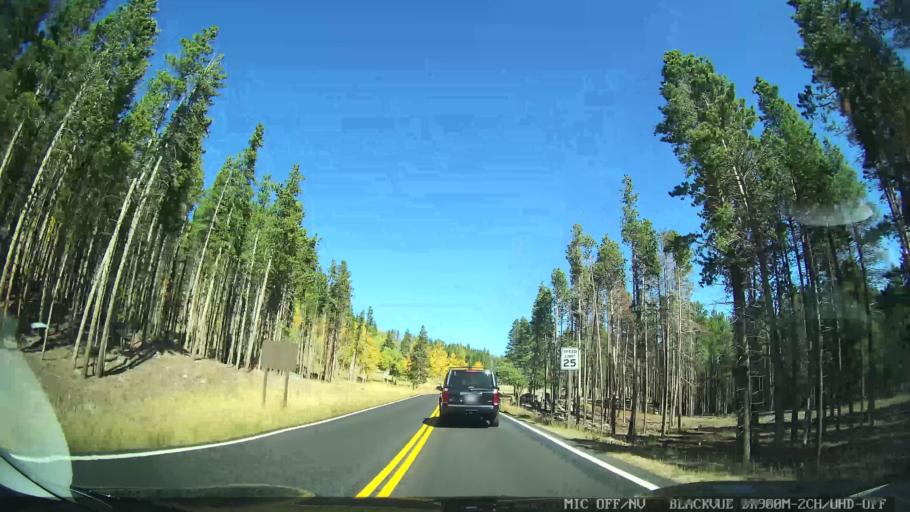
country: US
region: Colorado
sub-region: Larimer County
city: Estes Park
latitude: 40.3240
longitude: -105.6078
